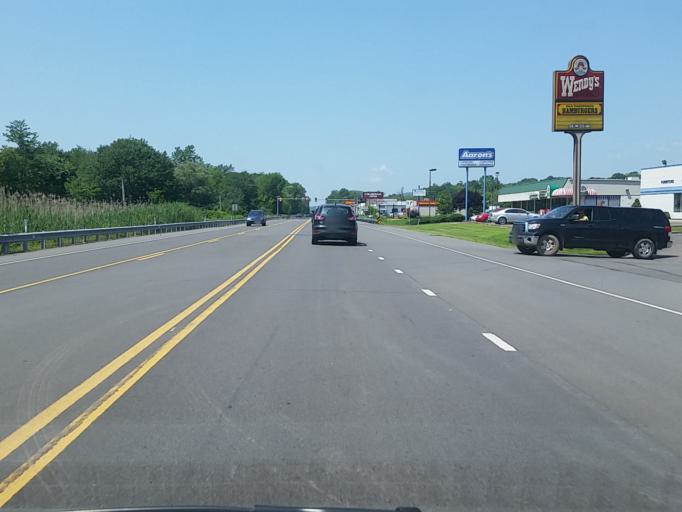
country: US
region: Pennsylvania
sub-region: Columbia County
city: Espy
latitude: 41.0092
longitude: -76.4208
